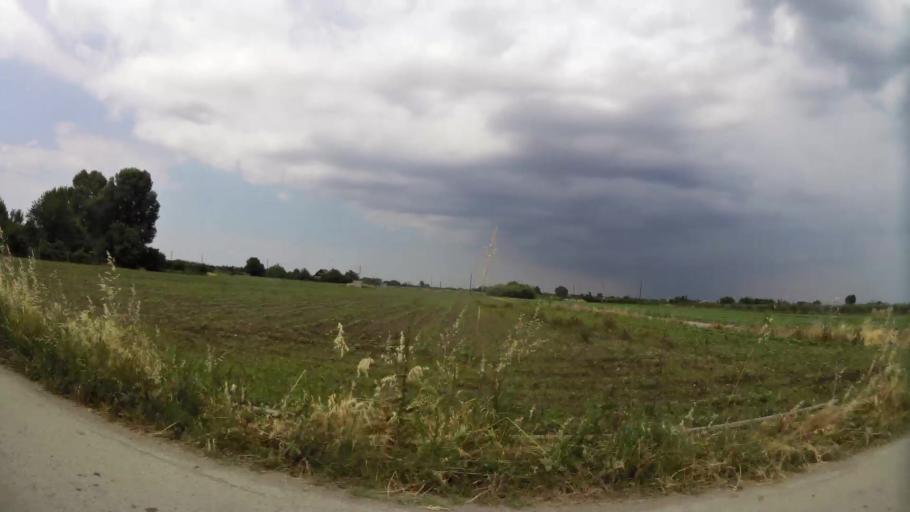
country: GR
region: Central Macedonia
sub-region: Nomos Pierias
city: Kallithea
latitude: 40.2765
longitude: 22.5828
